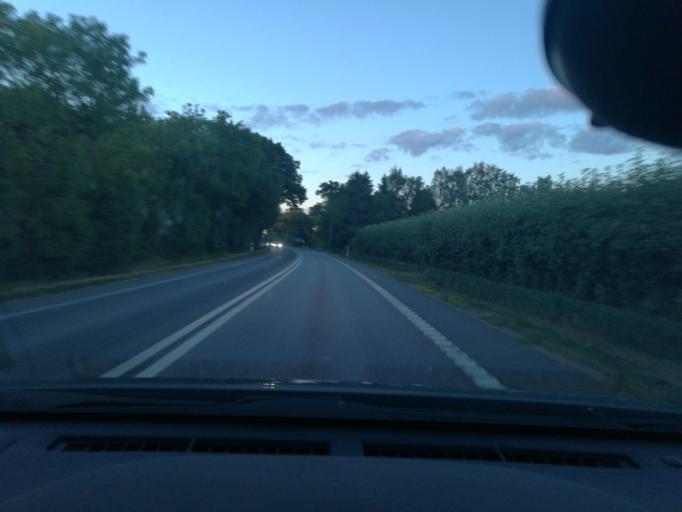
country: SE
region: Kalmar
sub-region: Borgholms Kommun
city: Borgholm
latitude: 56.7765
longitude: 16.5735
